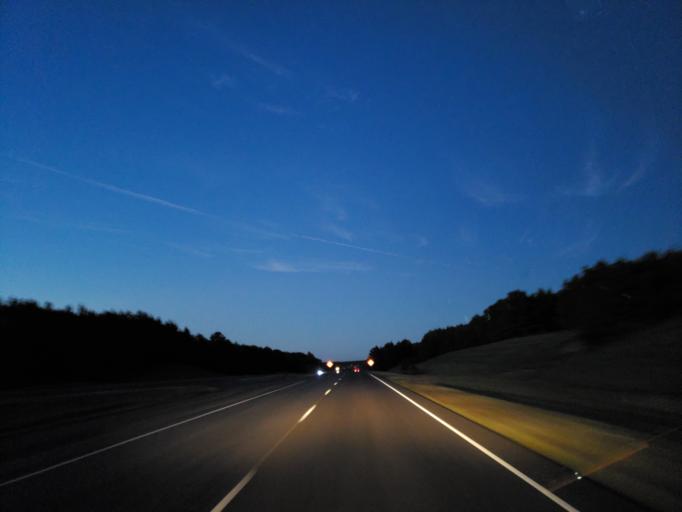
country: US
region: Mississippi
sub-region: Clarke County
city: Quitman
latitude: 32.0212
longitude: -88.6849
